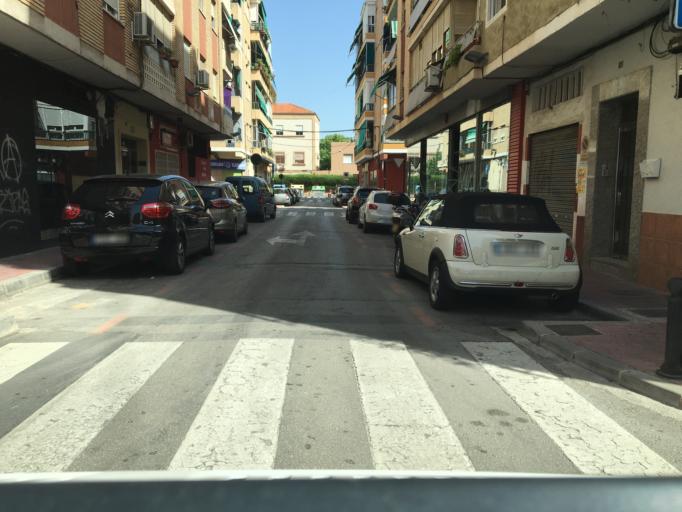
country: ES
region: Murcia
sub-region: Murcia
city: Murcia
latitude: 37.9960
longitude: -1.1282
